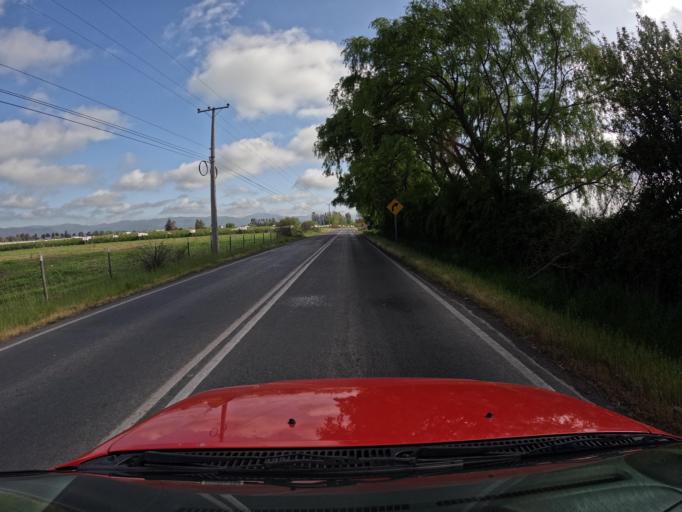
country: CL
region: Maule
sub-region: Provincia de Curico
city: Rauco
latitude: -34.8916
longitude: -71.2741
